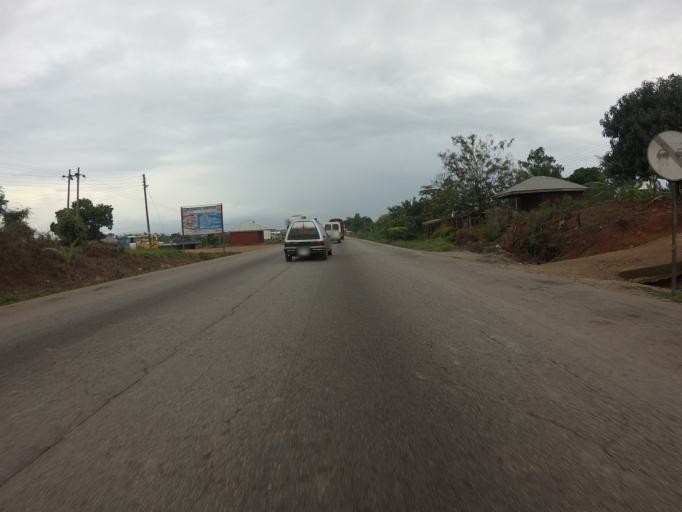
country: GH
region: Ashanti
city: Konongo
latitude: 6.6158
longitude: -1.1592
